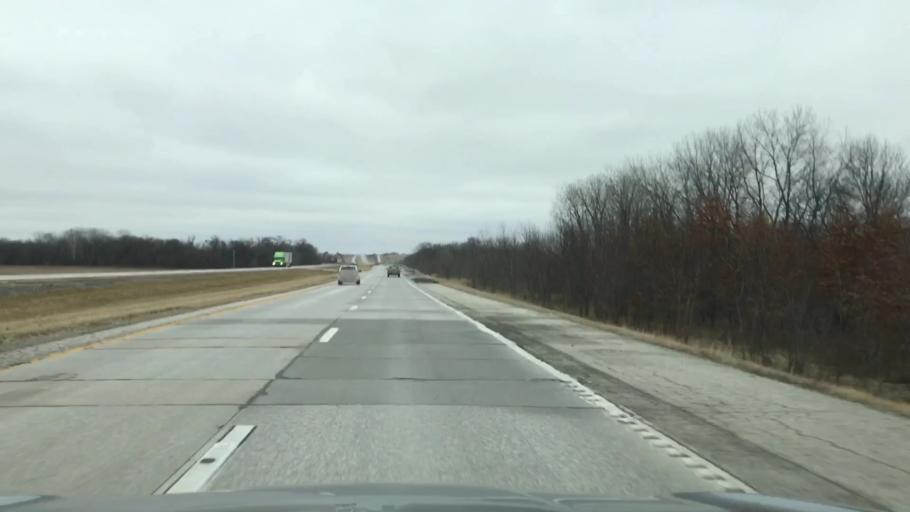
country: US
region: Missouri
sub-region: Linn County
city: Marceline
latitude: 39.7614
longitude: -92.9818
